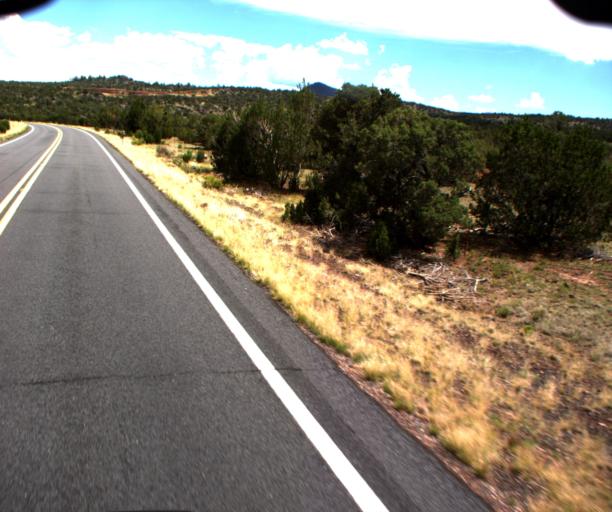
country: US
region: Arizona
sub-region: Coconino County
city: Parks
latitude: 35.5648
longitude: -111.9122
